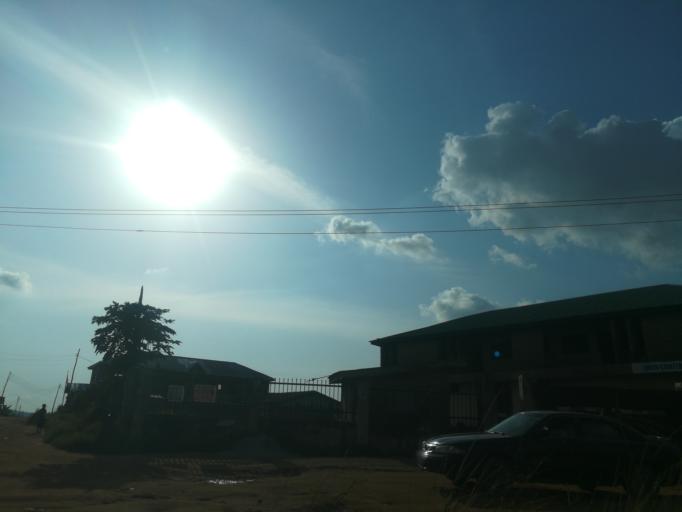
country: NG
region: Oyo
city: Ibadan
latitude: 7.3888
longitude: 3.8187
